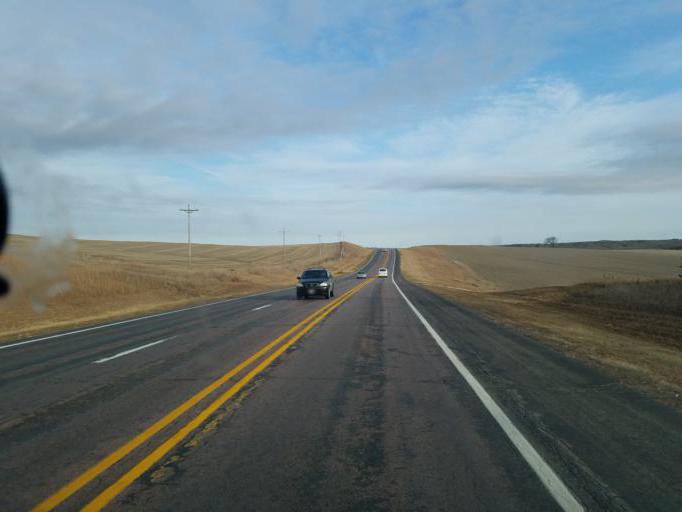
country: US
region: Nebraska
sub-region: Dixon County
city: Ponca
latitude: 42.4739
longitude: -96.6643
